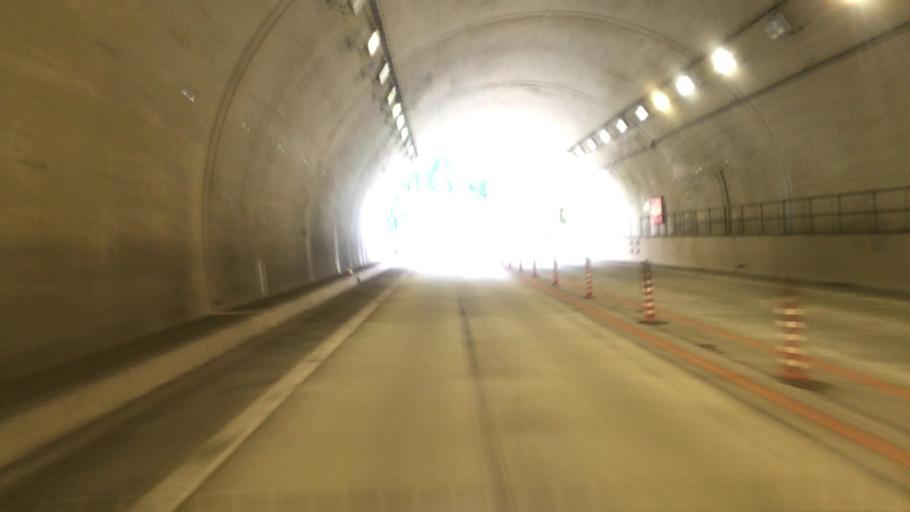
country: JP
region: Hyogo
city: Toyooka
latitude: 35.3469
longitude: 134.7890
